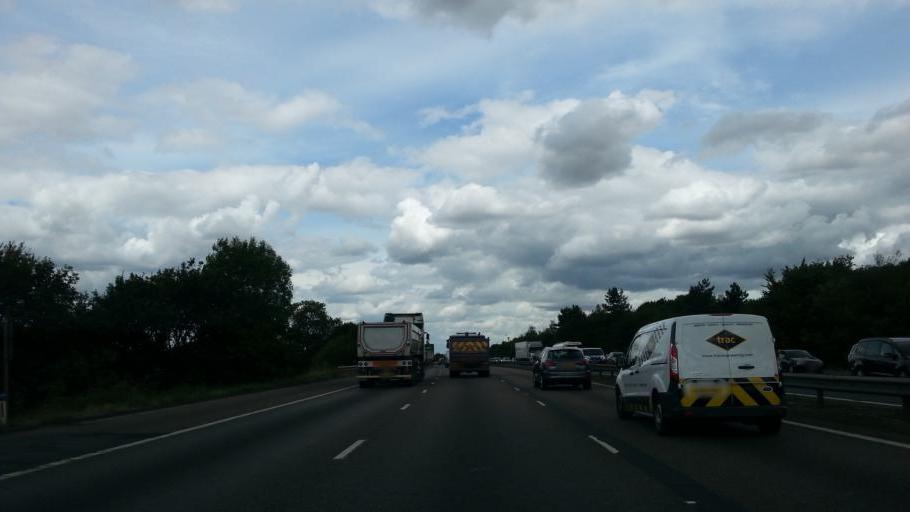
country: GB
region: England
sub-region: Essex
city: Epping
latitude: 51.7070
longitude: 0.1458
